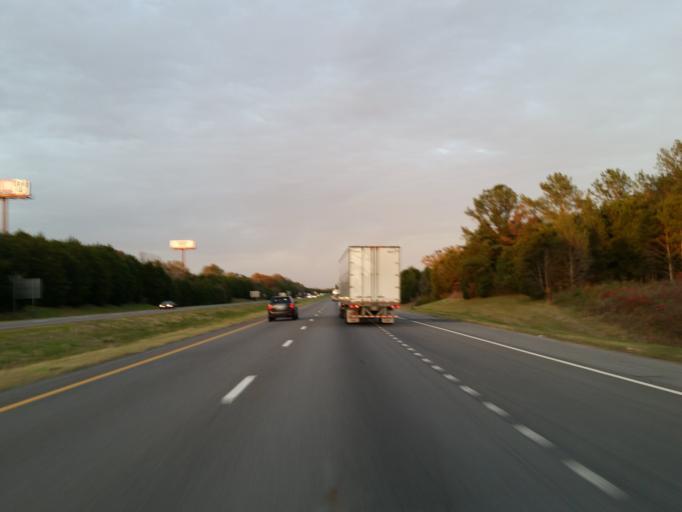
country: US
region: Alabama
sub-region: Sumter County
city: Livingston
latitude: 32.6302
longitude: -88.2055
